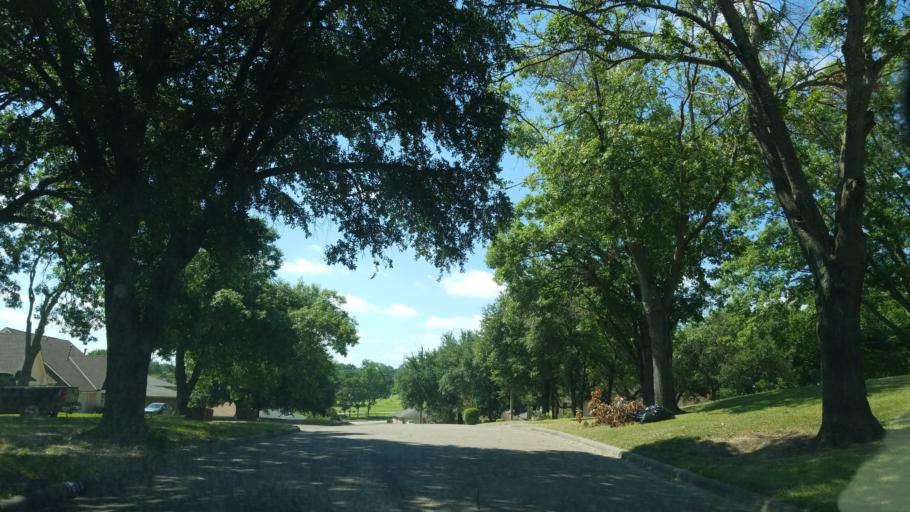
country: US
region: Texas
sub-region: Dallas County
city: Dallas
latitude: 32.7282
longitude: -96.7929
